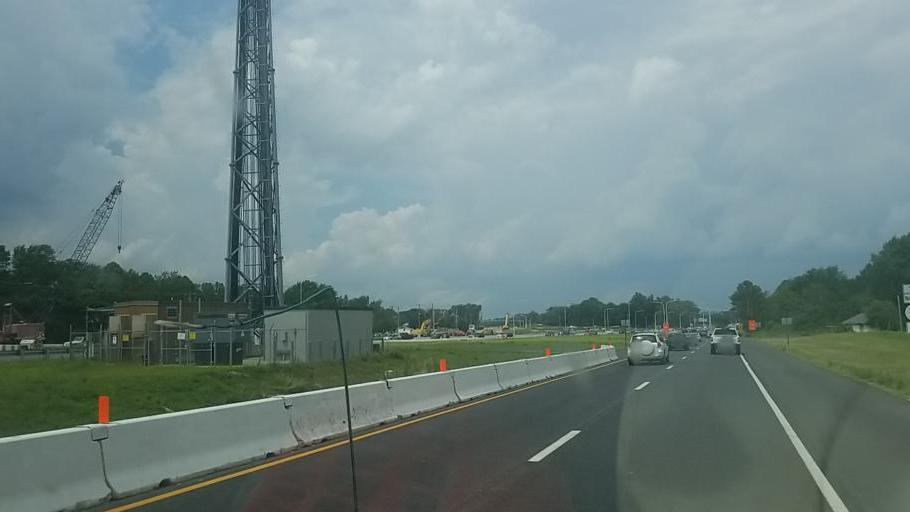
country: US
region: Delaware
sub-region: Kent County
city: Riverview
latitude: 39.0475
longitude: -75.4573
